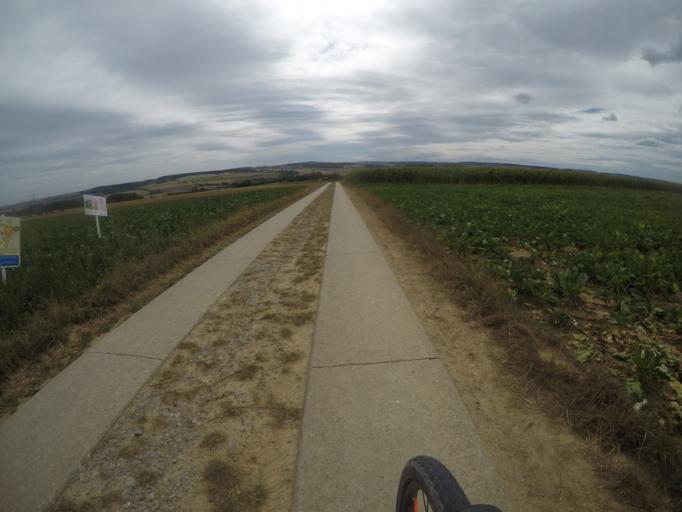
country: DE
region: Baden-Wuerttemberg
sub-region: Regierungsbezirk Stuttgart
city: Vaihingen an der Enz
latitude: 48.9365
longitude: 8.9927
